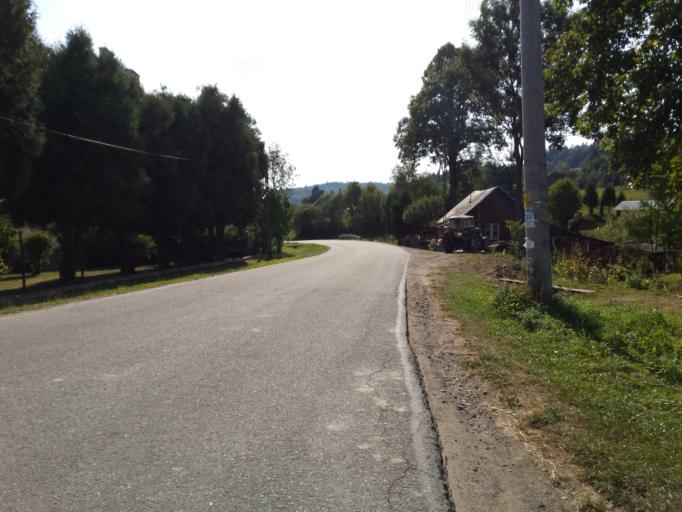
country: PL
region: Subcarpathian Voivodeship
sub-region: Powiat leski
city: Olszanica
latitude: 49.5365
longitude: 22.5056
